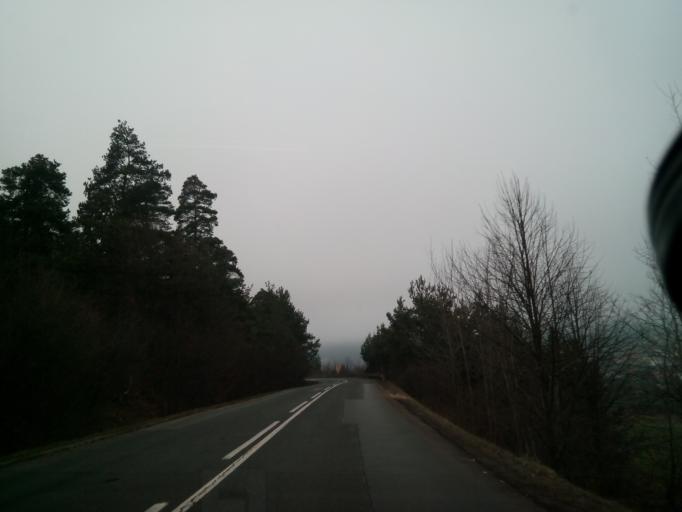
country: SK
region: Kosicky
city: Krompachy
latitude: 48.9207
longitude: 20.9260
